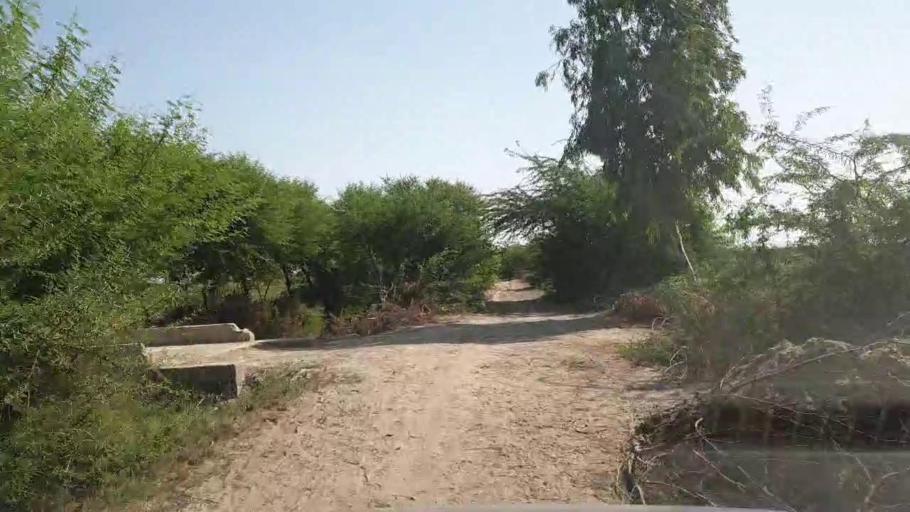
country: PK
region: Sindh
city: Kadhan
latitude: 24.5933
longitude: 69.0068
